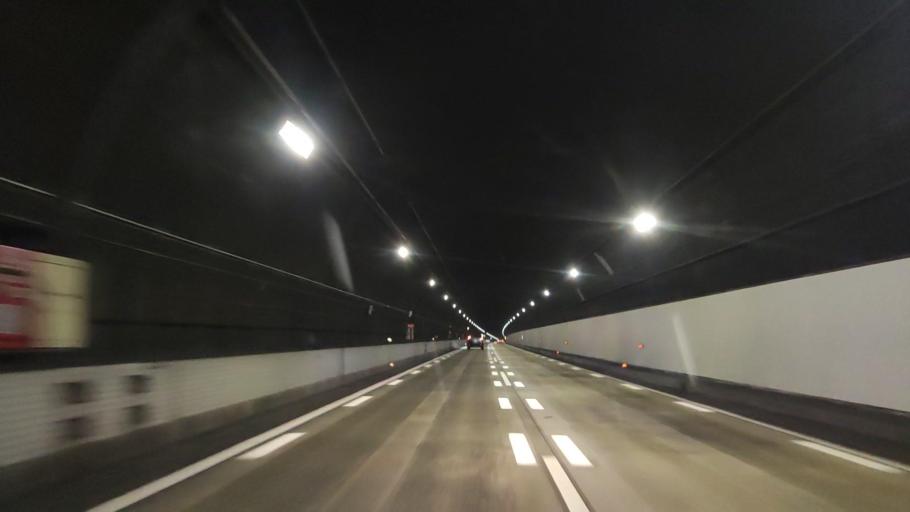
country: JP
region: Hiroshima
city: Fukuyama
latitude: 34.5033
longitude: 133.3266
